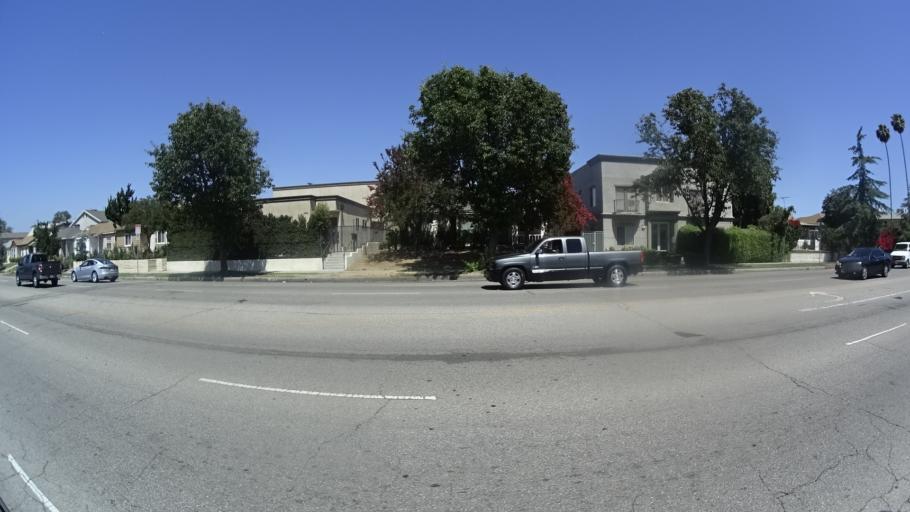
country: US
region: California
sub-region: Los Angeles County
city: Van Nuys
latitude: 34.1898
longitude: -118.5012
